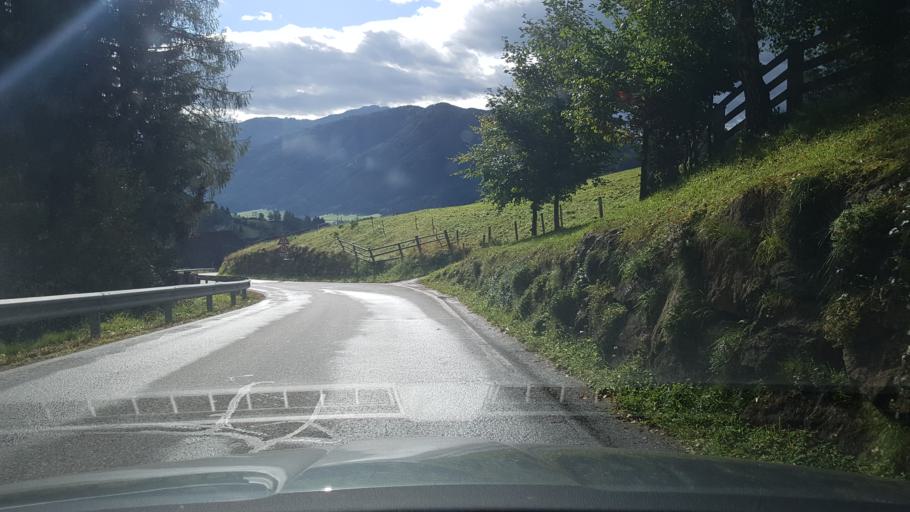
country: AT
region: Styria
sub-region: Politischer Bezirk Murau
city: Schoder
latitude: 47.2048
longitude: 14.1091
